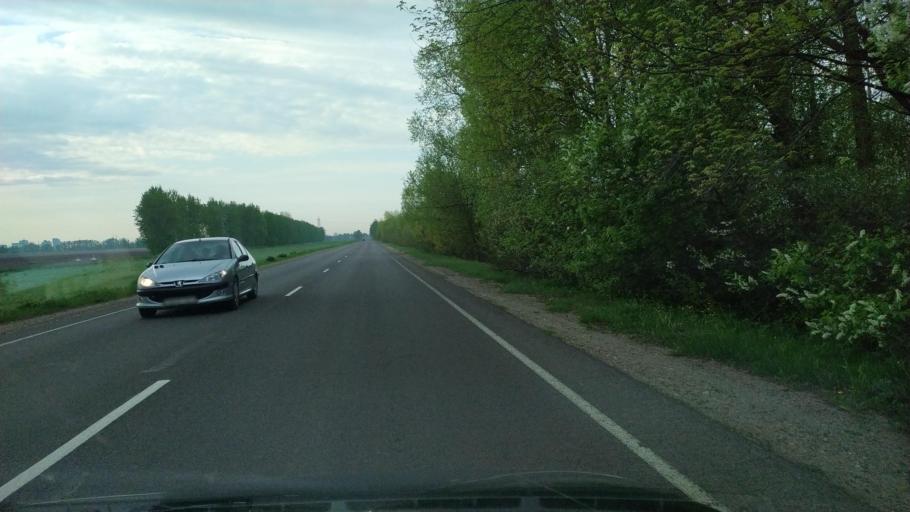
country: BY
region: Brest
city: Zhabinka
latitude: 52.2205
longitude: 23.9928
